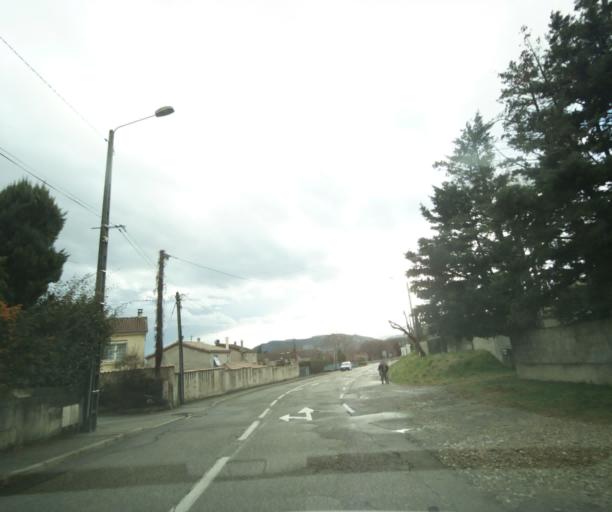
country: FR
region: Rhone-Alpes
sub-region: Departement de la Drome
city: Bourg-les-Valence
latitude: 44.9558
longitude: 4.9024
